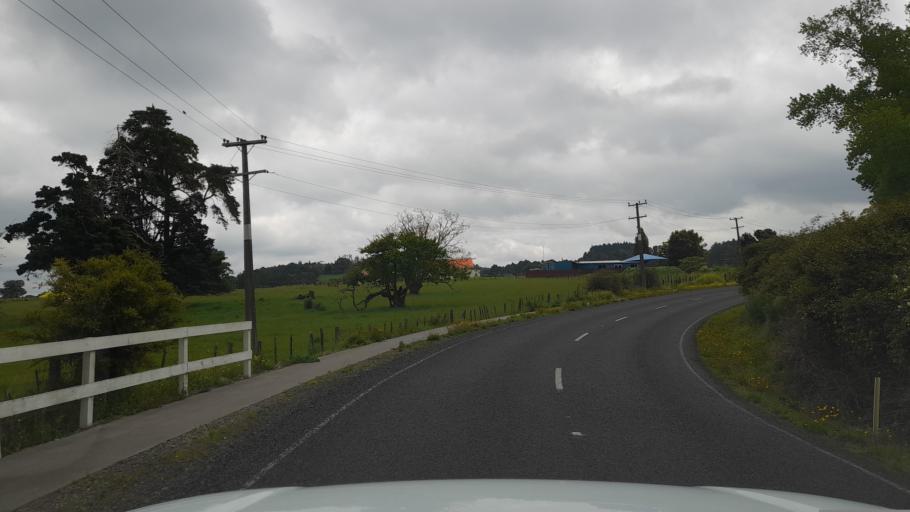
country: NZ
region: Northland
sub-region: Far North District
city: Waimate North
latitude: -35.4189
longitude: 173.7932
